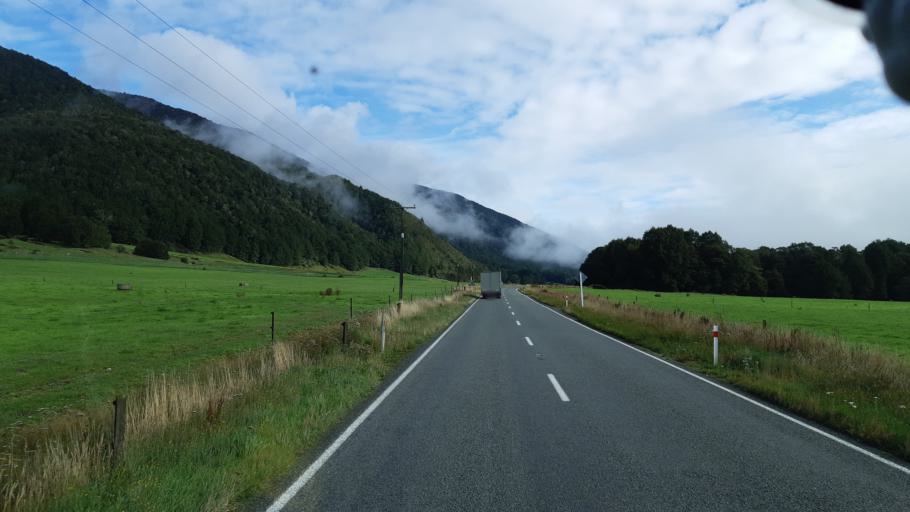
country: NZ
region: West Coast
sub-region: Buller District
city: Westport
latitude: -42.0487
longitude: 172.2558
